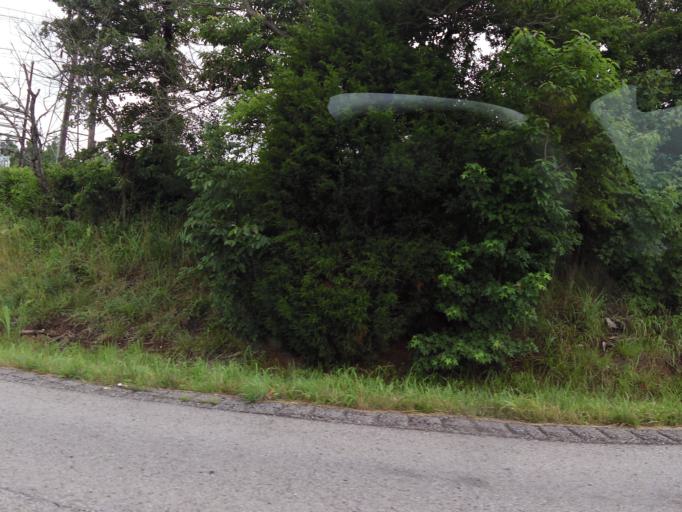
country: US
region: Kentucky
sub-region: Hopkins County
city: Madisonville
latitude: 37.3232
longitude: -87.3744
